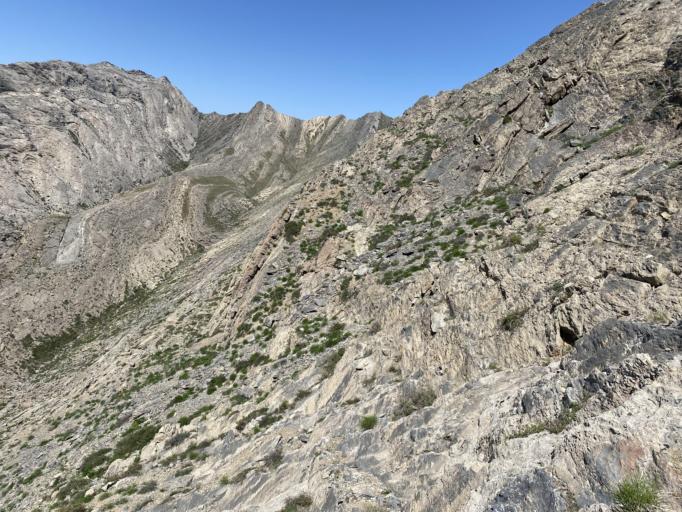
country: KZ
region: Ongtustik Qazaqstan
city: Kentau
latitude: 43.9549
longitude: 68.2628
